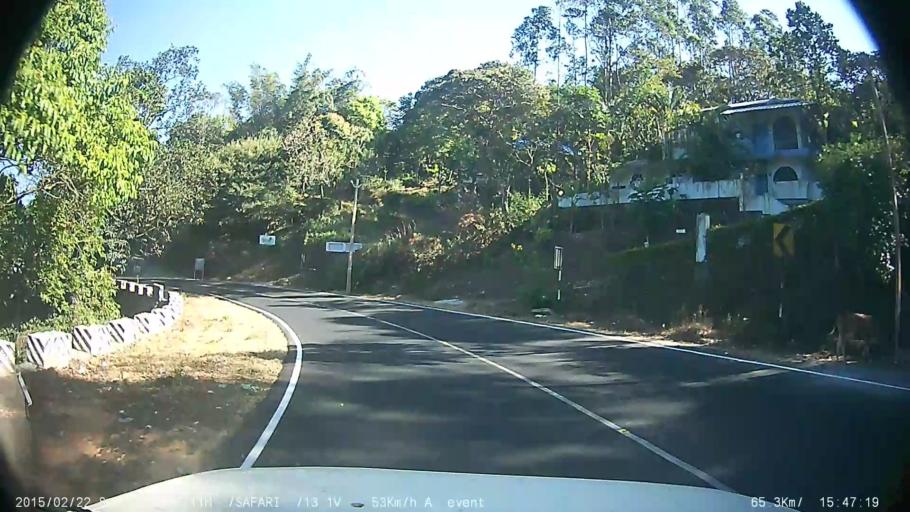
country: IN
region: Kerala
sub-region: Kottayam
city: Erattupetta
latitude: 9.5777
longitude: 76.9895
